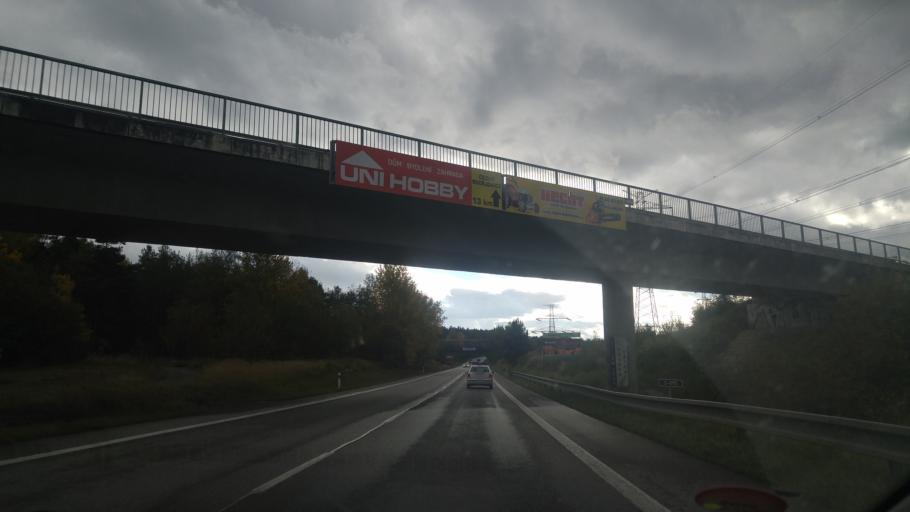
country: CZ
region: Jihocesky
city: Sevetin
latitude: 49.0942
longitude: 14.5586
